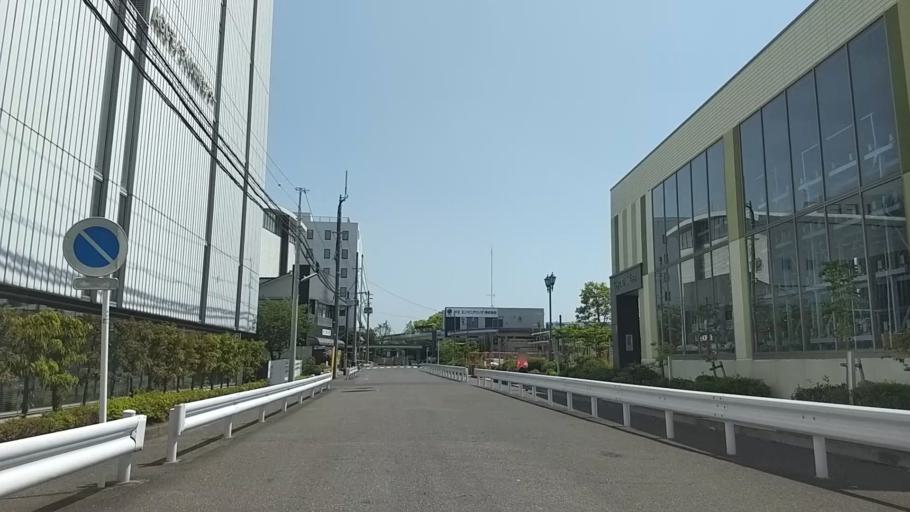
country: JP
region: Kanagawa
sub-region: Kawasaki-shi
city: Kawasaki
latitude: 35.4960
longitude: 139.6889
